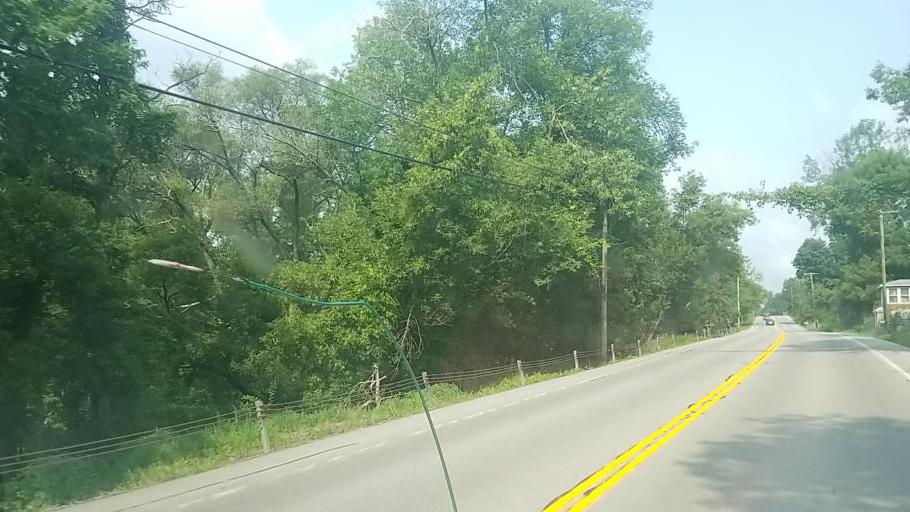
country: US
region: New York
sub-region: Montgomery County
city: Fort Plain
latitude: 42.9775
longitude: -74.6379
